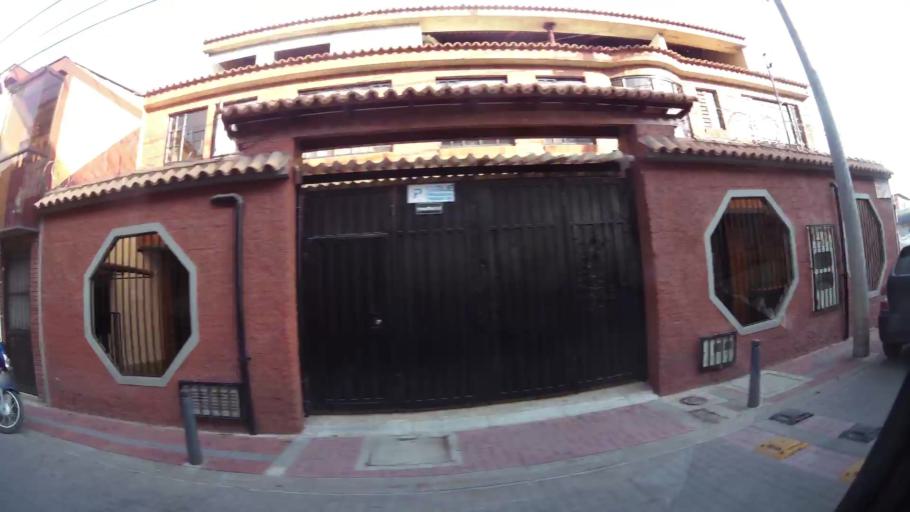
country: CO
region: Cundinamarca
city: Cota
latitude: 4.8095
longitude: -74.1032
